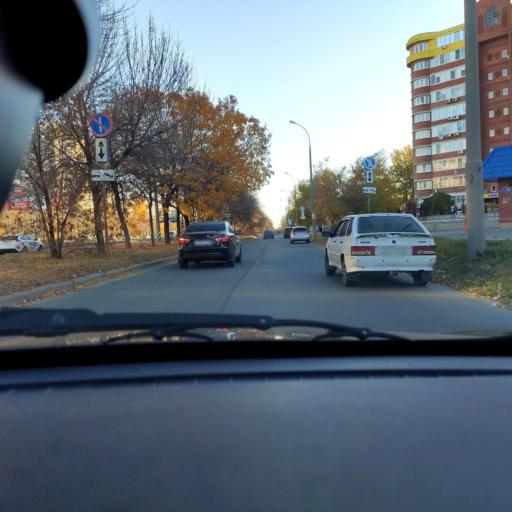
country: RU
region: Samara
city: Tol'yatti
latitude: 53.5190
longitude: 49.3144
